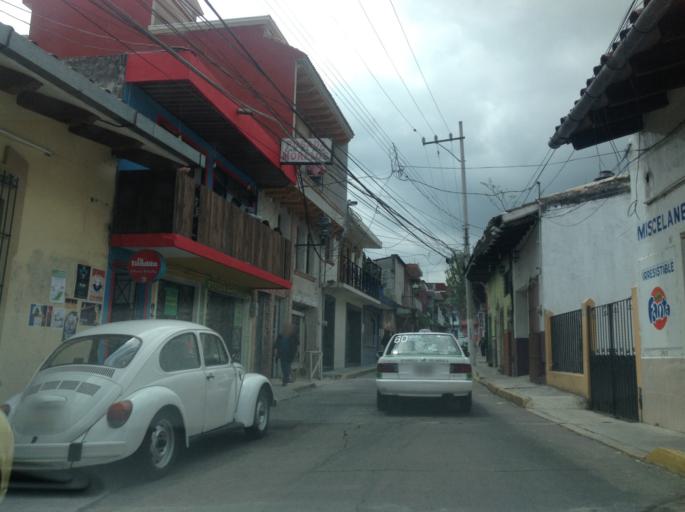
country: MX
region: Veracruz
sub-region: Xalapa
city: Xalapa de Enriquez
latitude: 19.5244
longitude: -96.9221
